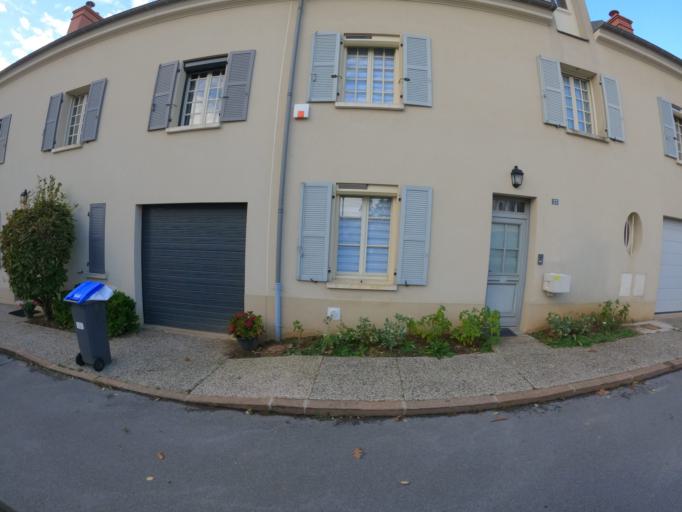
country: FR
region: Ile-de-France
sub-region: Departement de Seine-et-Marne
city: Magny-le-Hongre
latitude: 48.8772
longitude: 2.8116
